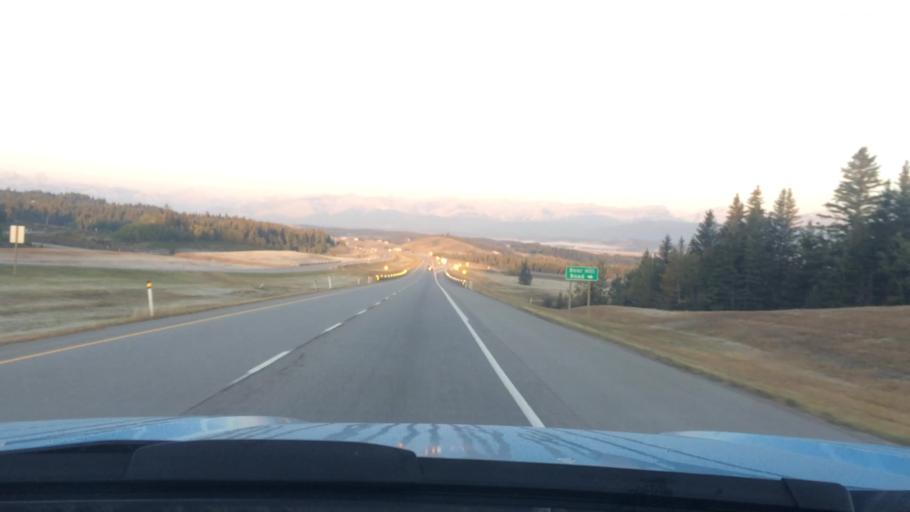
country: CA
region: Alberta
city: Cochrane
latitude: 51.1623
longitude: -114.7651
